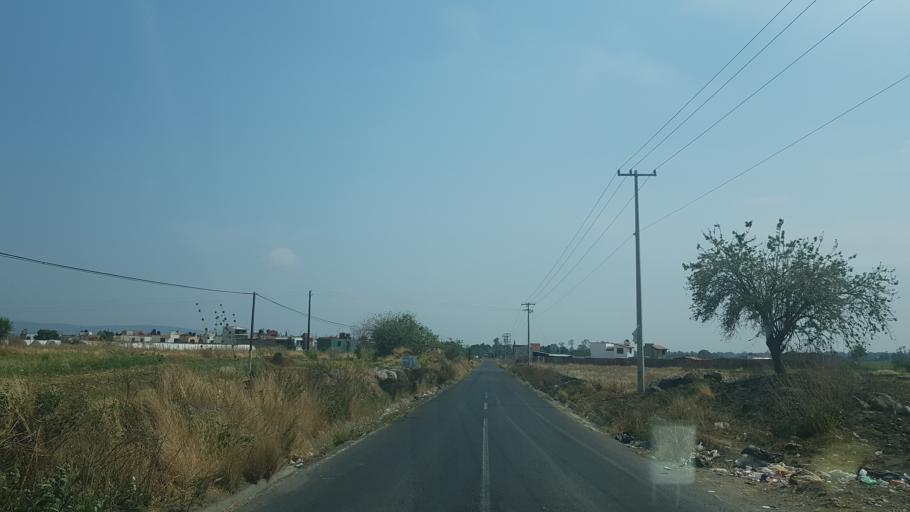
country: MX
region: Puebla
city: San Juan Tianguismanalco
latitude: 18.9323
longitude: -98.4543
